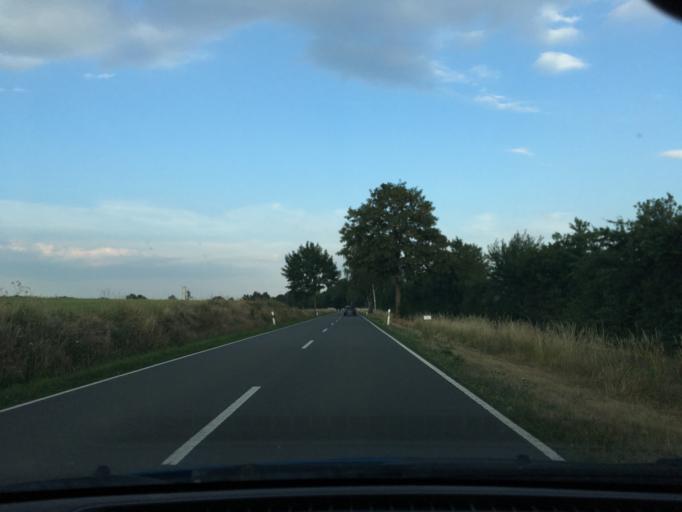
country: DE
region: Lower Saxony
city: Eschede
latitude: 52.7277
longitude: 10.2477
